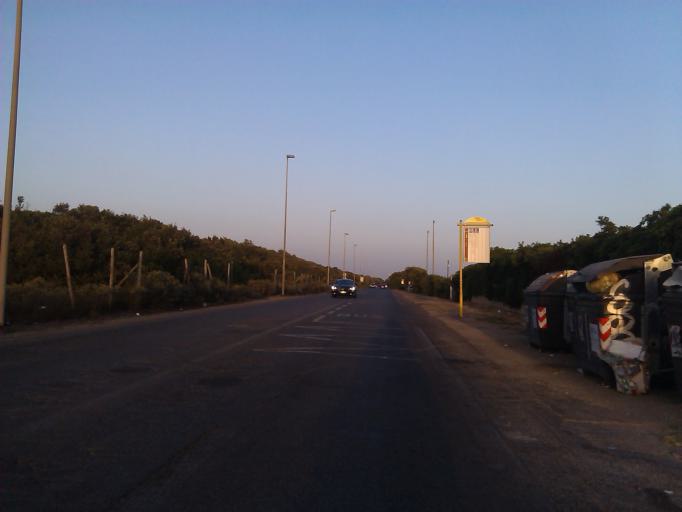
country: IT
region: Latium
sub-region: Citta metropolitana di Roma Capitale
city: Acilia-Castel Fusano-Ostia Antica
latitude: 41.7119
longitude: 12.3259
